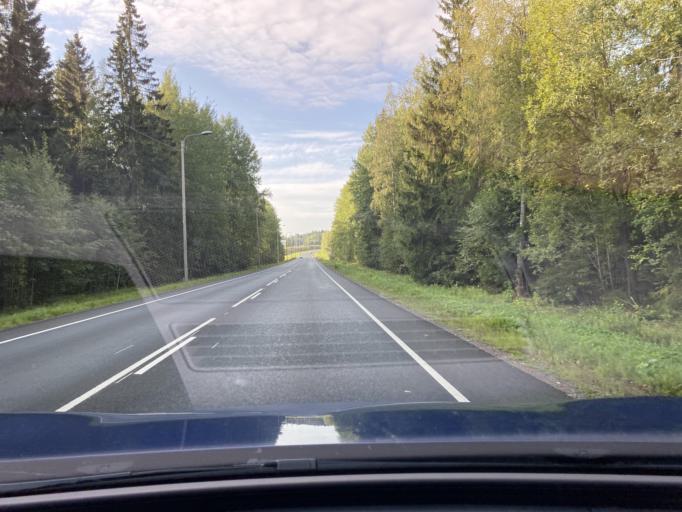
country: FI
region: Kymenlaakso
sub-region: Kouvola
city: Kouvola
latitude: 60.8924
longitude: 26.6043
